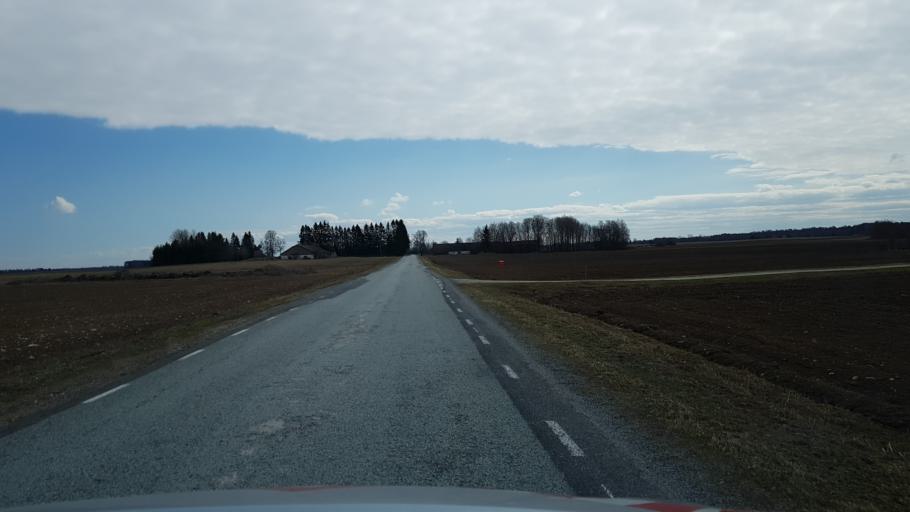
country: EE
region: Laeaene-Virumaa
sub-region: Haljala vald
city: Haljala
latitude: 59.4208
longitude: 26.2369
